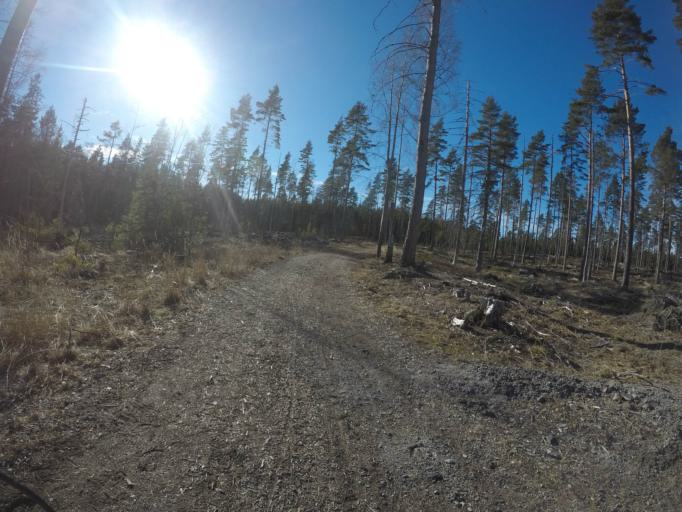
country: SE
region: Soedermanland
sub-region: Eskilstuna Kommun
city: Torshalla
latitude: 59.4253
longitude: 16.4411
